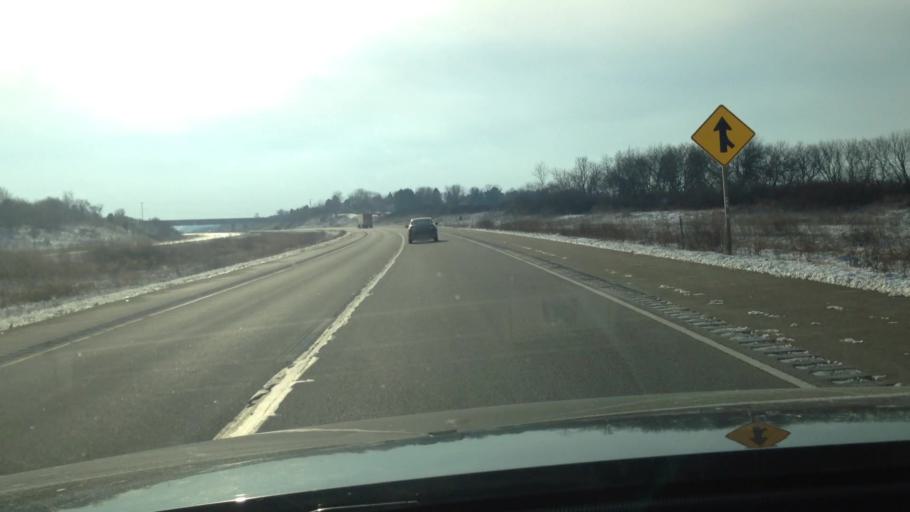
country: US
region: Wisconsin
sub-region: Walworth County
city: East Troy
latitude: 42.7468
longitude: -88.4476
